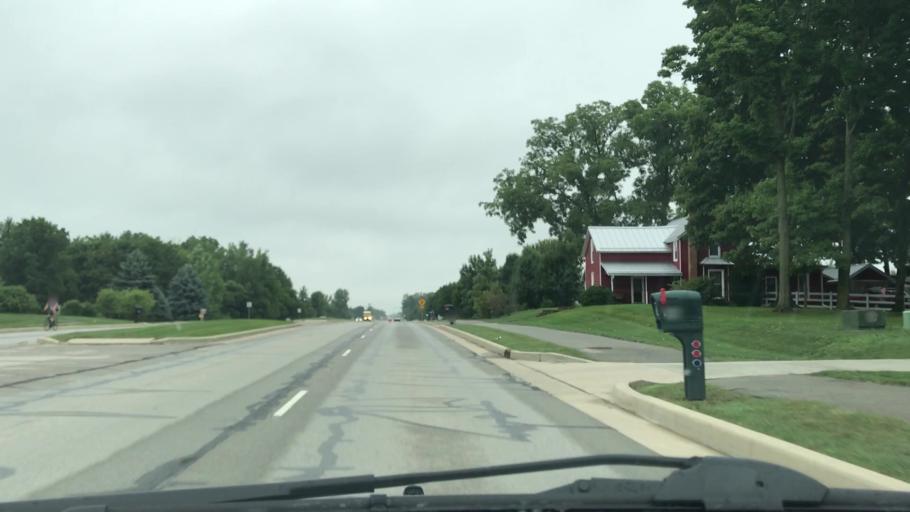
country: US
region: Indiana
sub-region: Hamilton County
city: Carmel
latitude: 40.0166
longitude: -86.0705
